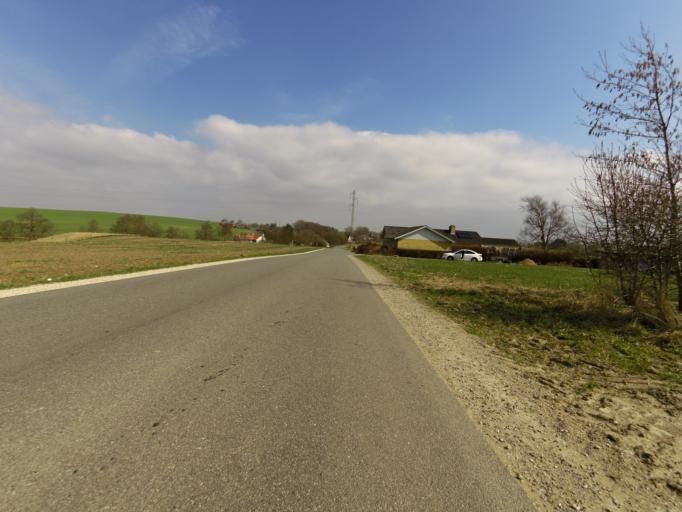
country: DK
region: Central Jutland
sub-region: Struer Kommune
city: Struer
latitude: 56.4386
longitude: 8.6521
